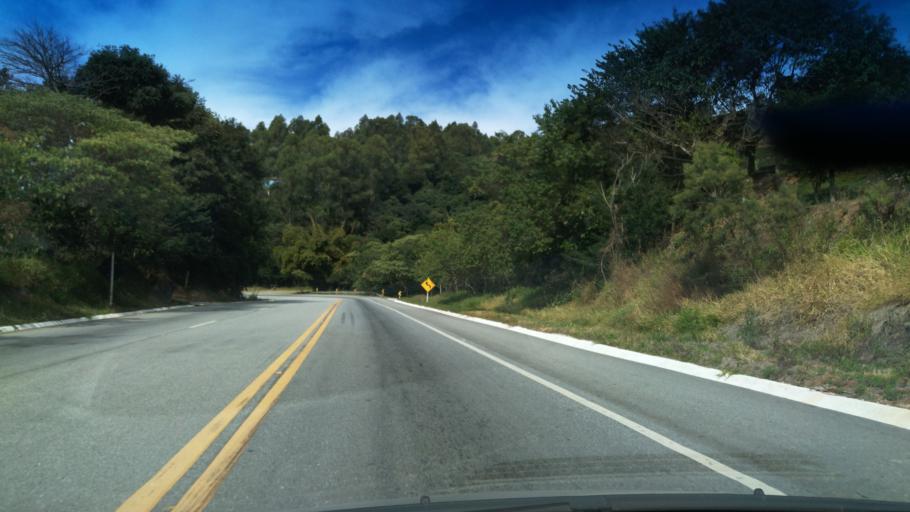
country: BR
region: Minas Gerais
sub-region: Borda Da Mata
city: Borda da Mata
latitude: -22.1333
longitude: -46.1496
